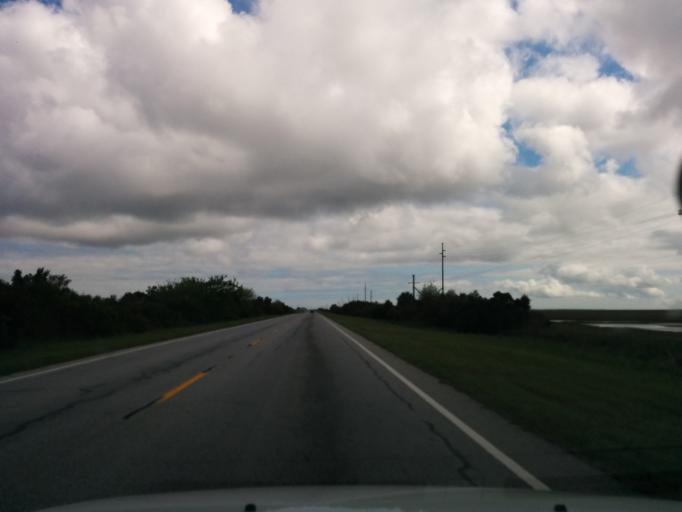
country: US
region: Georgia
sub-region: Glynn County
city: Brunswick
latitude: 31.0945
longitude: -81.4845
